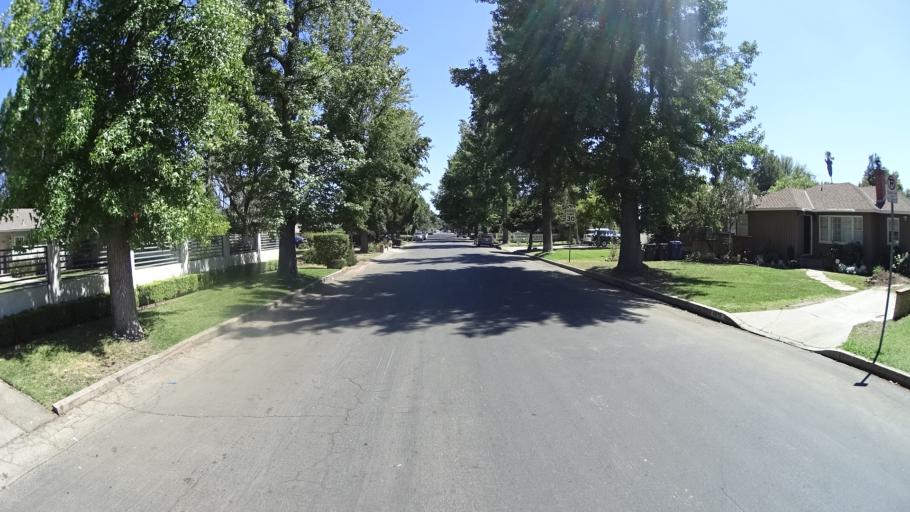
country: US
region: California
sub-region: Los Angeles County
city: Van Nuys
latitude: 34.1910
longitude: -118.4705
